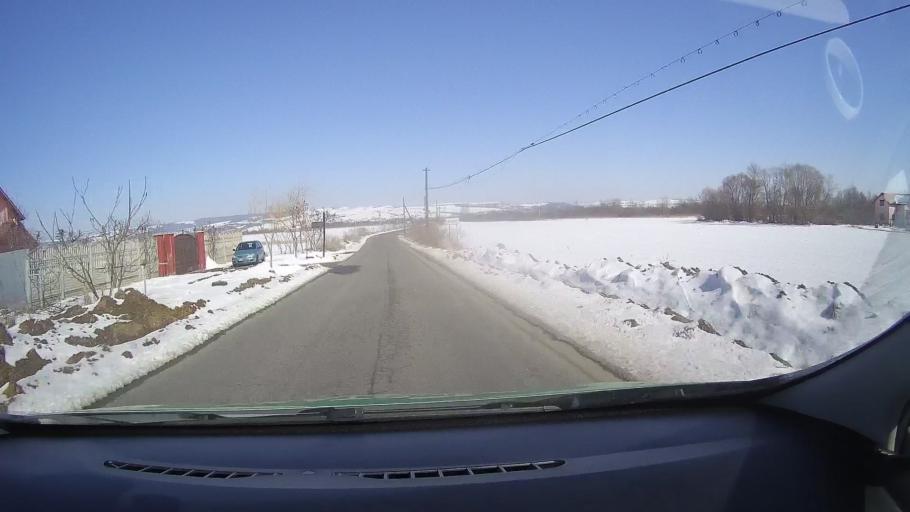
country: RO
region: Brasov
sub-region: Comuna Mandra
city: Mandra
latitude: 45.8274
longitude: 25.0108
